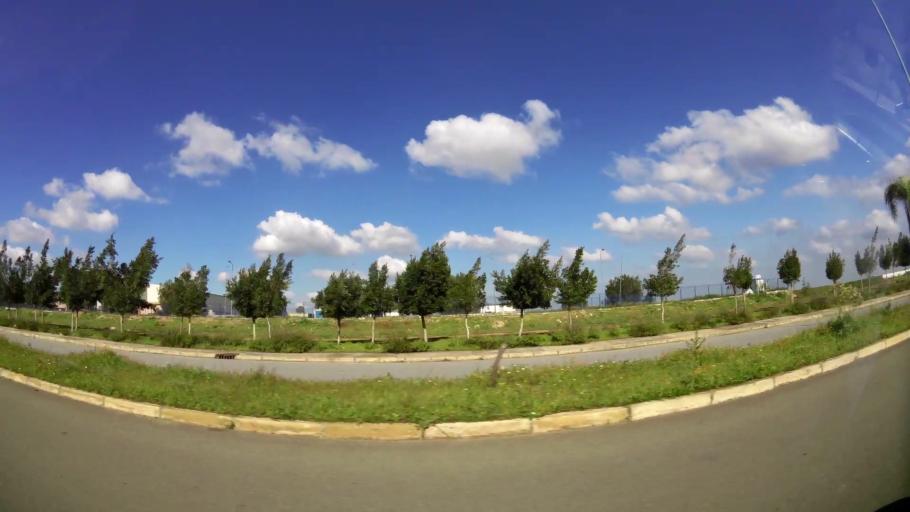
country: MA
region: Grand Casablanca
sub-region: Mediouna
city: Mediouna
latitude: 33.4009
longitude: -7.5555
